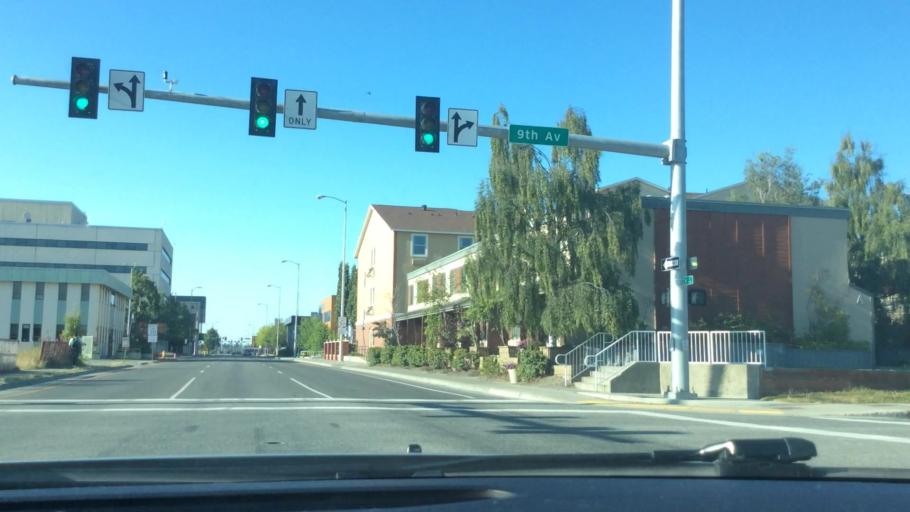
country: US
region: Alaska
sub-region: Anchorage Municipality
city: Anchorage
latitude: 61.2135
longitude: -149.8833
